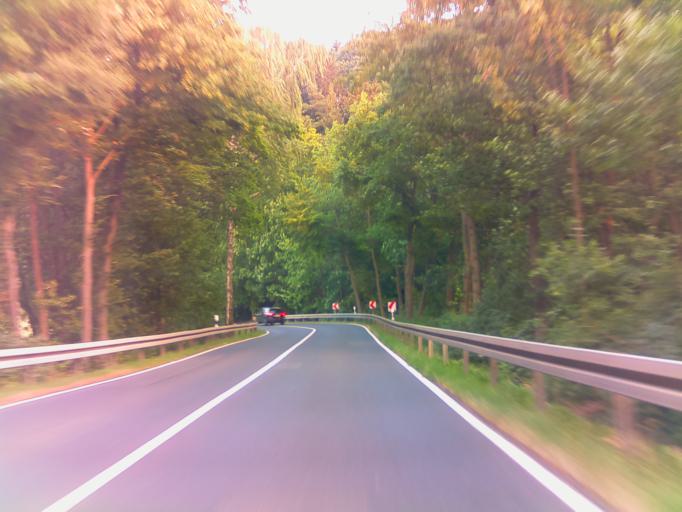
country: DE
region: Thuringia
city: Blankenhain
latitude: 50.8480
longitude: 11.3370
